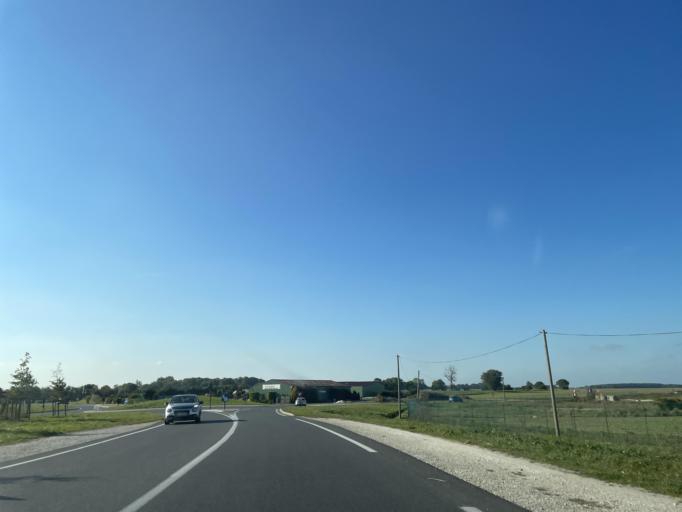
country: FR
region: Ile-de-France
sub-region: Departement de Seine-et-Marne
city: La Celle-sur-Morin
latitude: 48.8361
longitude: 2.9892
